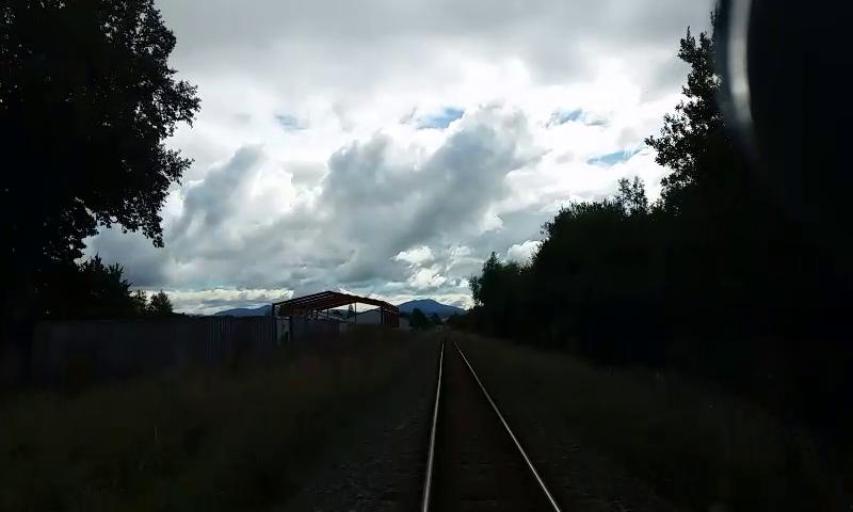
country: NZ
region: Canterbury
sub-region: Waimakariri District
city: Woodend
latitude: -43.3148
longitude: 172.6011
